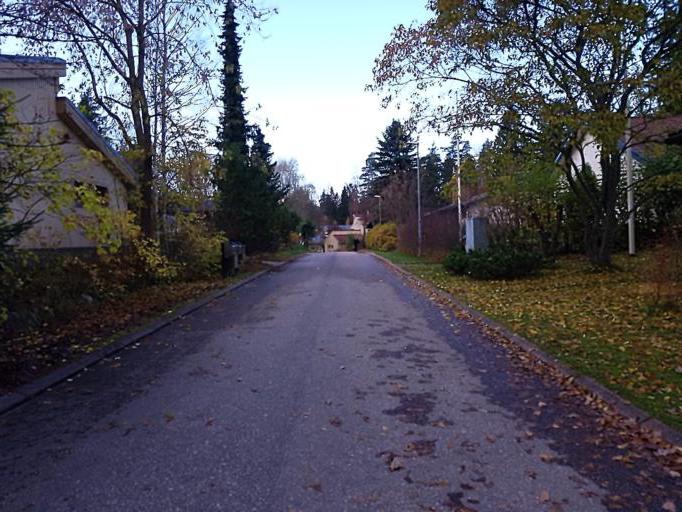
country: FI
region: Uusimaa
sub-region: Helsinki
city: Teekkarikylae
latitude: 60.2564
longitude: 24.8882
